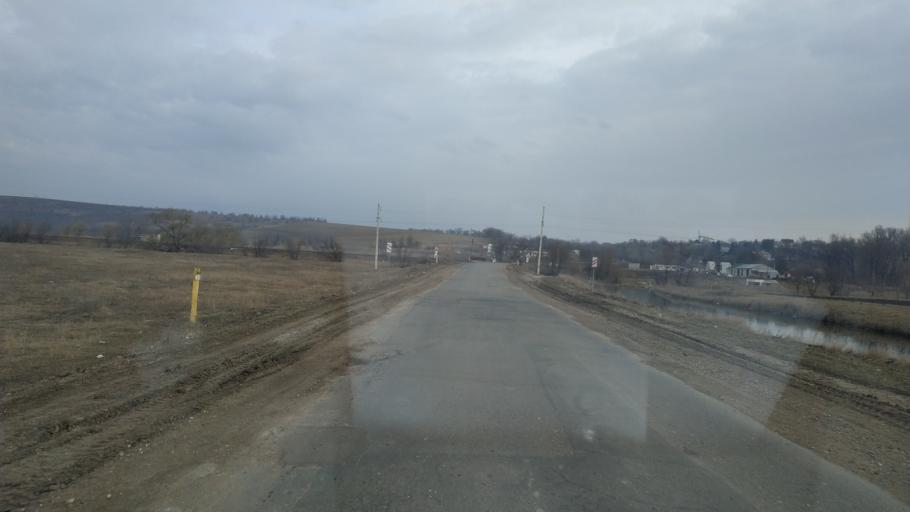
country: MD
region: Chisinau
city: Singera
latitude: 46.9219
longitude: 29.0466
